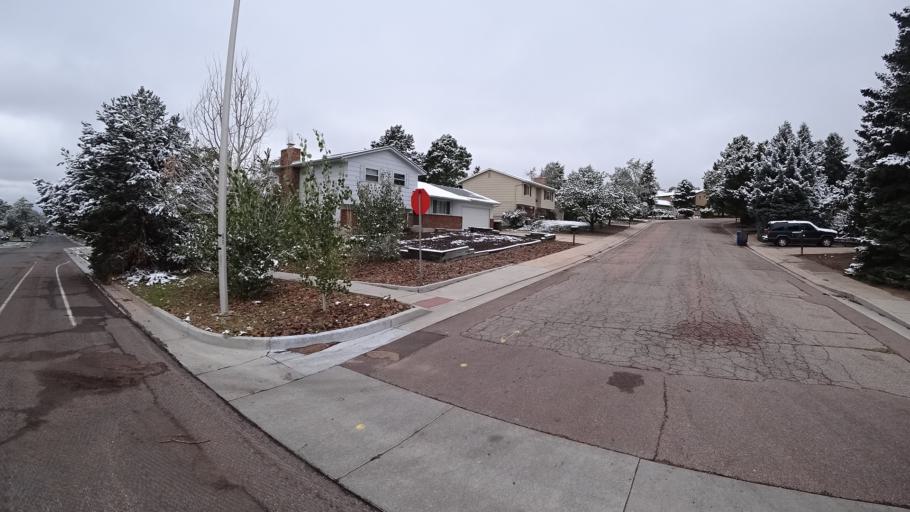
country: US
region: Colorado
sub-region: El Paso County
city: Cimarron Hills
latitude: 38.9084
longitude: -104.7621
